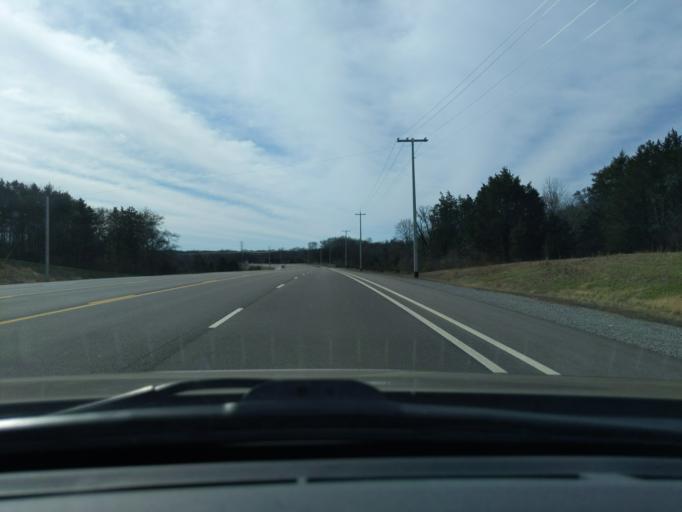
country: US
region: Tennessee
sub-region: Wilson County
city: Mount Juliet
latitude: 36.2077
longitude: -86.4972
